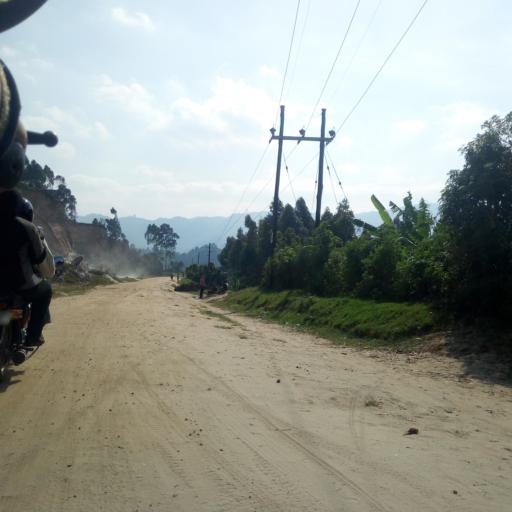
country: UG
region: Western Region
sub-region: Kisoro District
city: Kisoro
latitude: -1.2293
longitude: 29.7109
